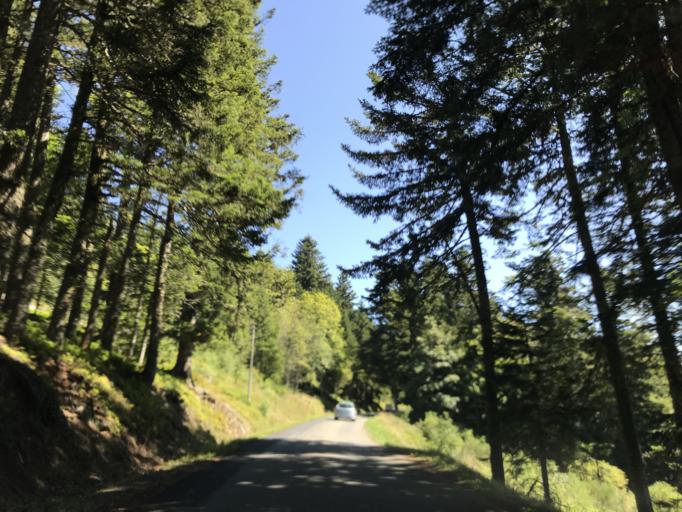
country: FR
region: Auvergne
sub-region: Departement du Puy-de-Dome
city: Job
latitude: 45.6811
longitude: 3.7608
